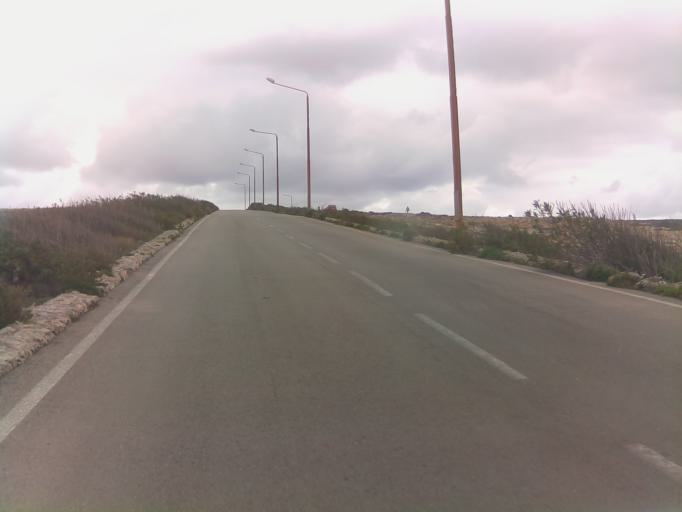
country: MT
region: Il-Mellieha
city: Mellieha
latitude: 35.9850
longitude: 14.3349
